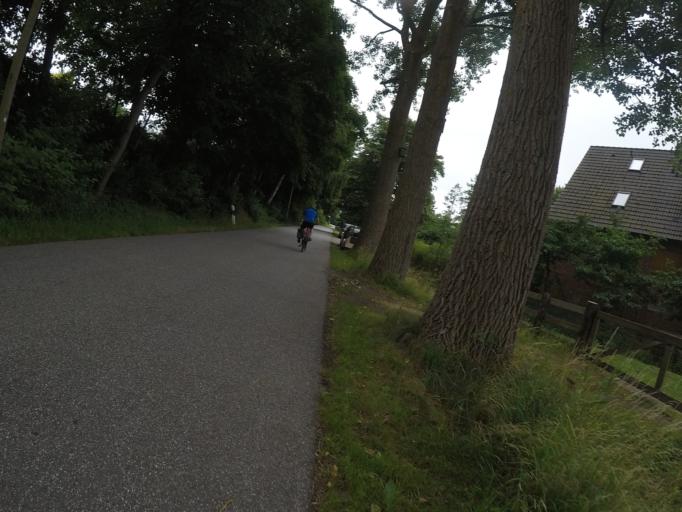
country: DE
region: Lower Saxony
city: Neu Wulmstorf
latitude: 53.5272
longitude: 9.8477
